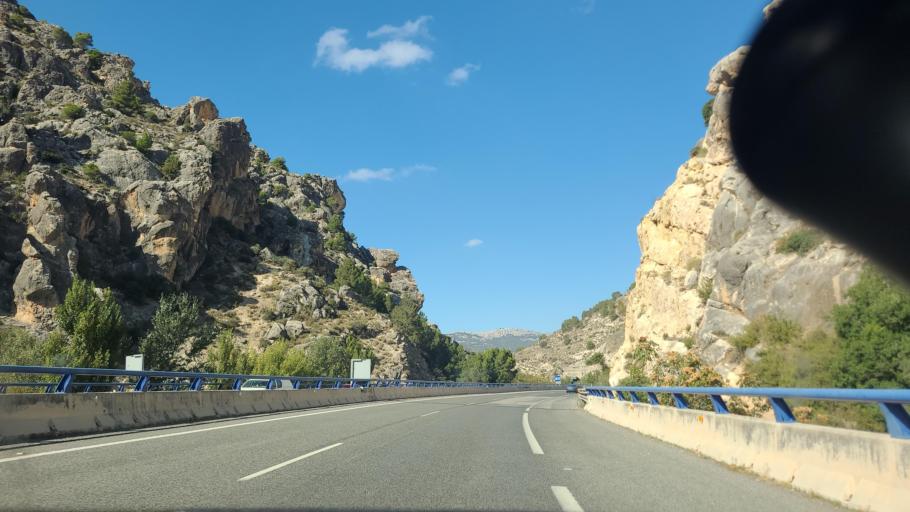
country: ES
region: Andalusia
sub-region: Provincia de Jaen
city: Pegalajar
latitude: 37.6850
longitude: -3.6292
